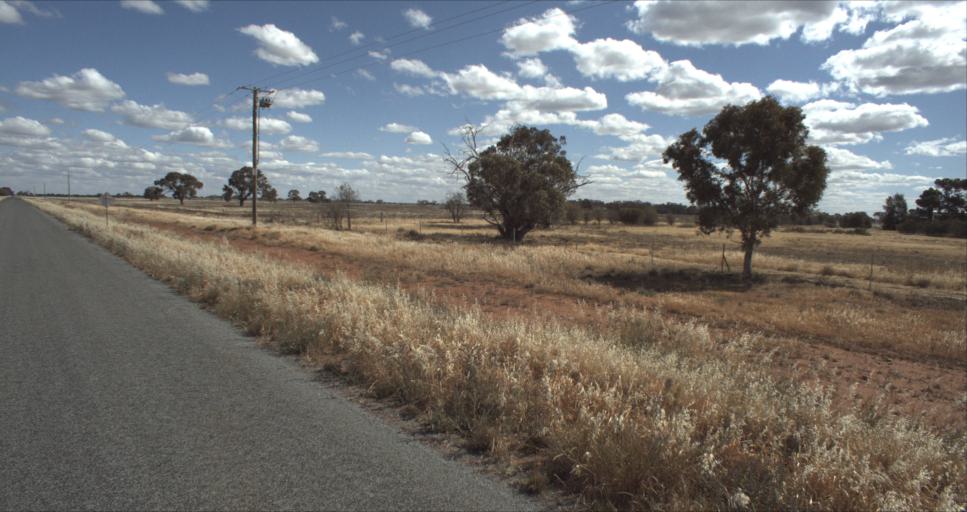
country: AU
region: New South Wales
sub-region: Leeton
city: Leeton
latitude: -34.4605
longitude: 146.2528
